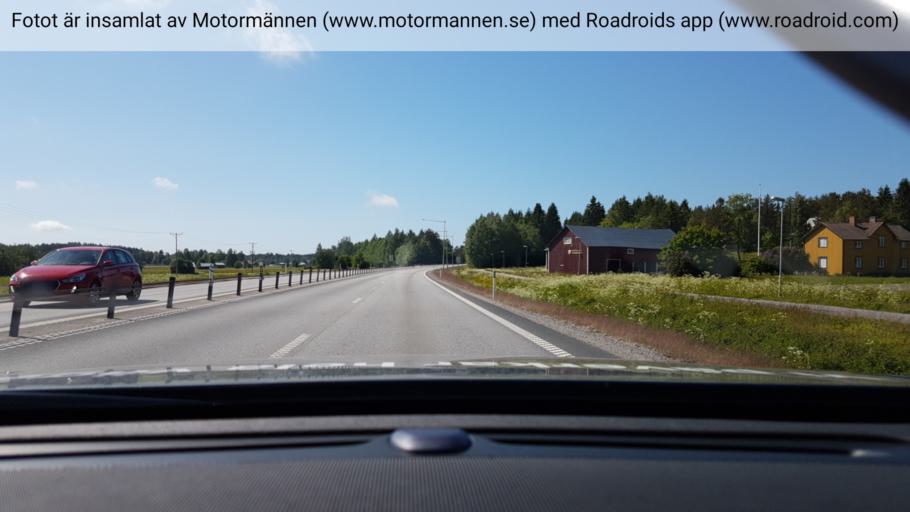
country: SE
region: Vaesterbotten
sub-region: Umea Kommun
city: Roback
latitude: 63.7728
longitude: 20.1837
